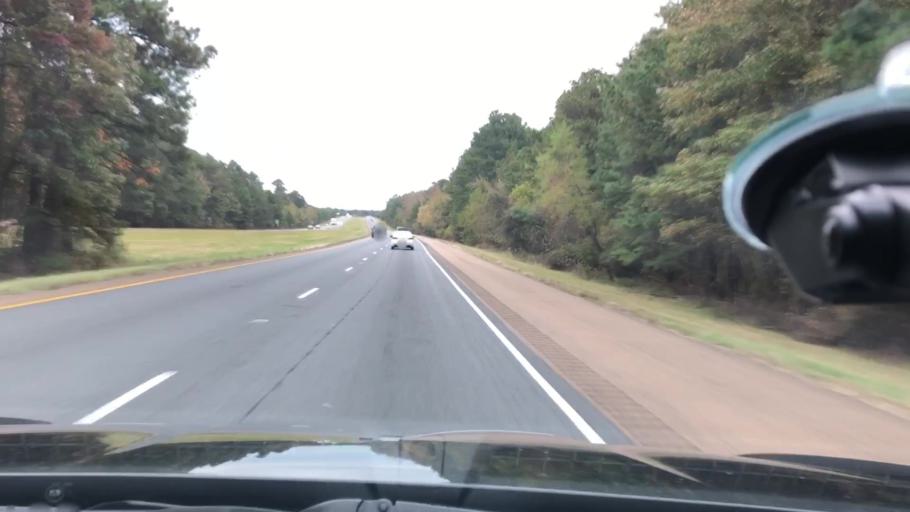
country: US
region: Arkansas
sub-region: Clark County
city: Gurdon
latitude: 33.9435
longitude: -93.2418
